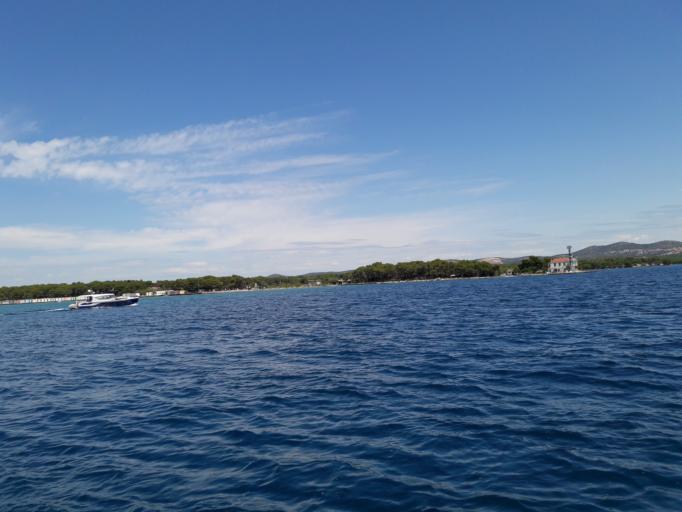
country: HR
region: Sibensko-Kniniska
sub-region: Grad Sibenik
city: Sibenik
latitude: 43.7189
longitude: 15.8473
